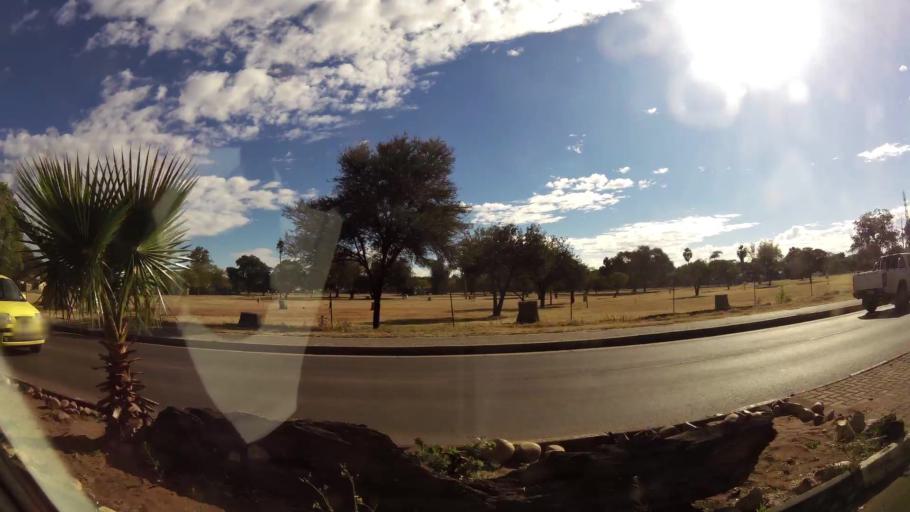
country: ZA
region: Limpopo
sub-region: Waterberg District Municipality
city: Warmbaths
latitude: -24.8854
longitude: 28.2883
